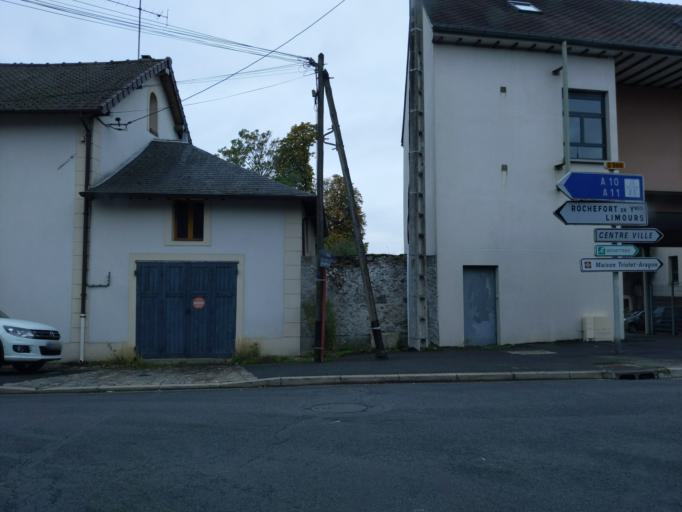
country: FR
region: Ile-de-France
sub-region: Departement des Yvelines
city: Saint-Arnoult-en-Yvelines
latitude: 48.5730
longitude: 1.9423
